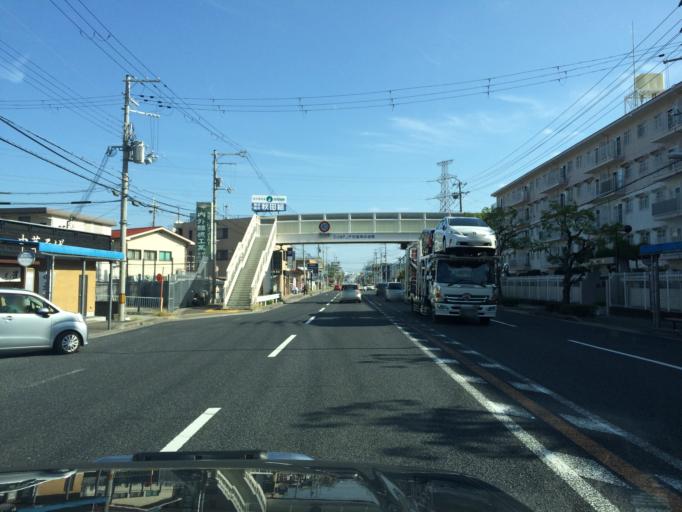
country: JP
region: Hyogo
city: Takarazuka
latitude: 34.7982
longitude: 135.3710
